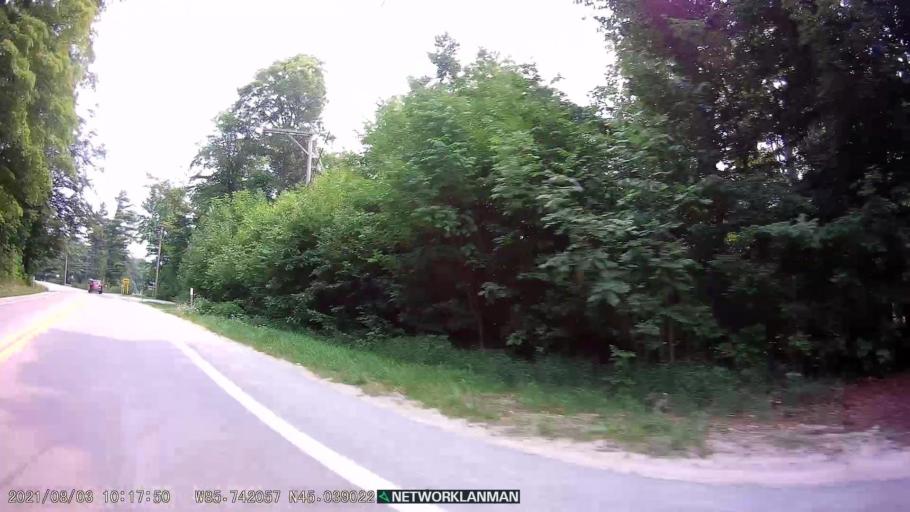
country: US
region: Michigan
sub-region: Leelanau County
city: Leland
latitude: 45.0434
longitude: -85.7389
